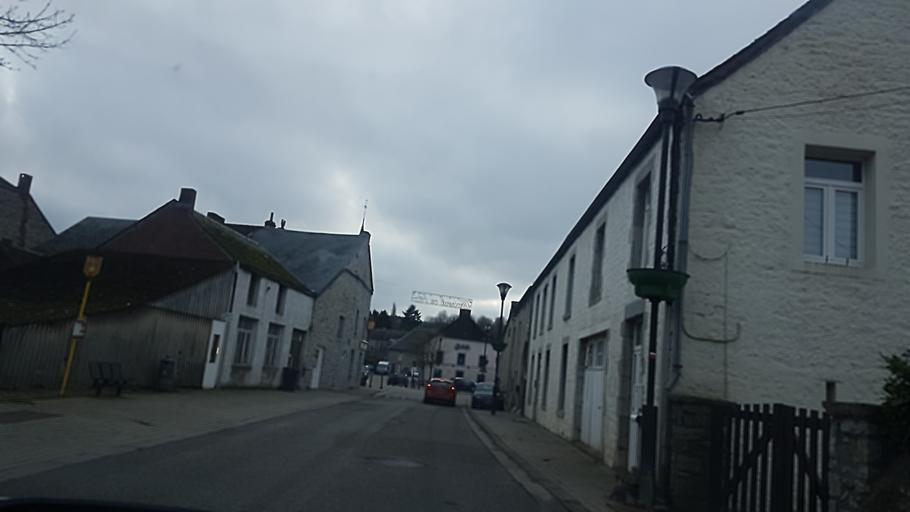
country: BE
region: Wallonia
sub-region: Province de Namur
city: Couvin
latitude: 50.0747
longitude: 4.6067
